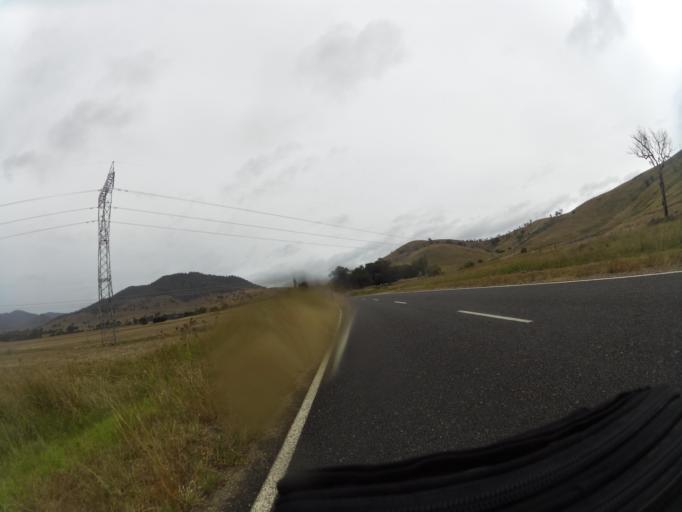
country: AU
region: New South Wales
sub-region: Greater Hume Shire
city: Holbrook
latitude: -36.2092
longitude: 147.7342
